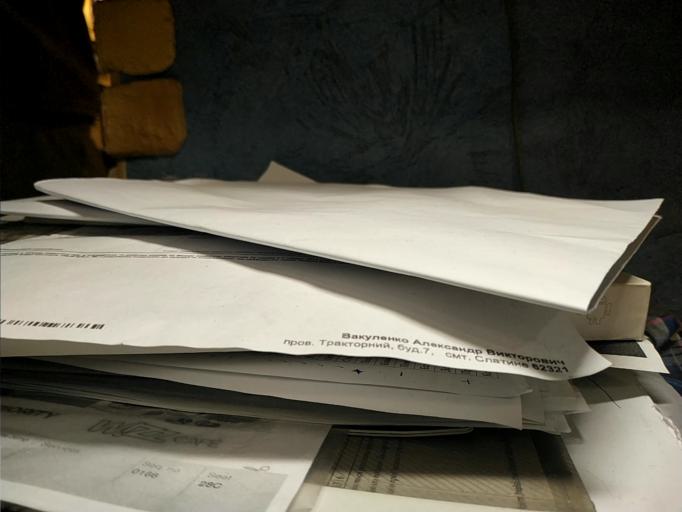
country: RU
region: Tverskaya
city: Zubtsov
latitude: 56.0997
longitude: 34.6906
